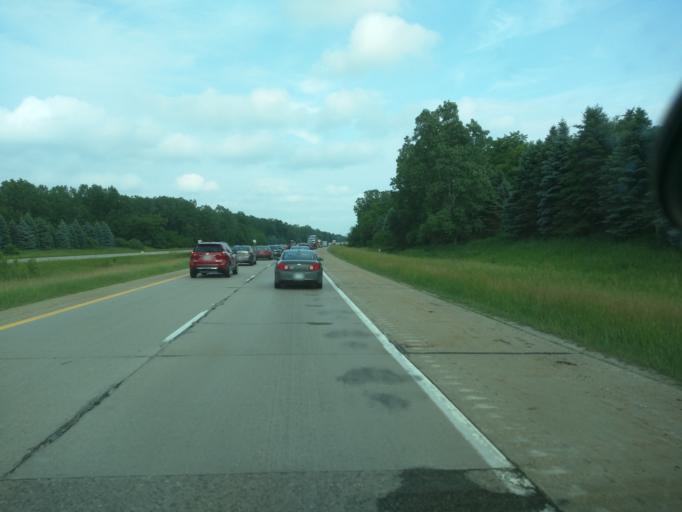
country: US
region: Michigan
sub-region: Clinton County
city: Bath
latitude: 42.8027
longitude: -84.4673
